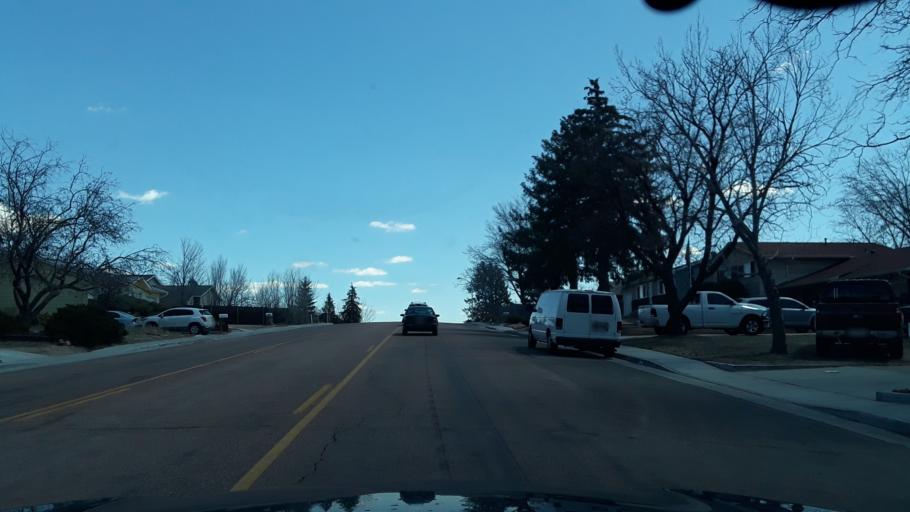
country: US
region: Colorado
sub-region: El Paso County
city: Cimarron Hills
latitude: 38.8462
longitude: -104.7063
